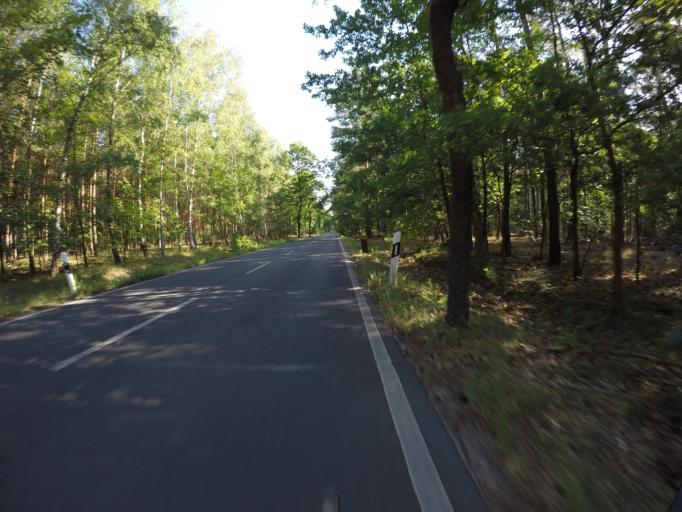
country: DE
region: Berlin
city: Schmockwitz
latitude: 52.3541
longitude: 13.6487
